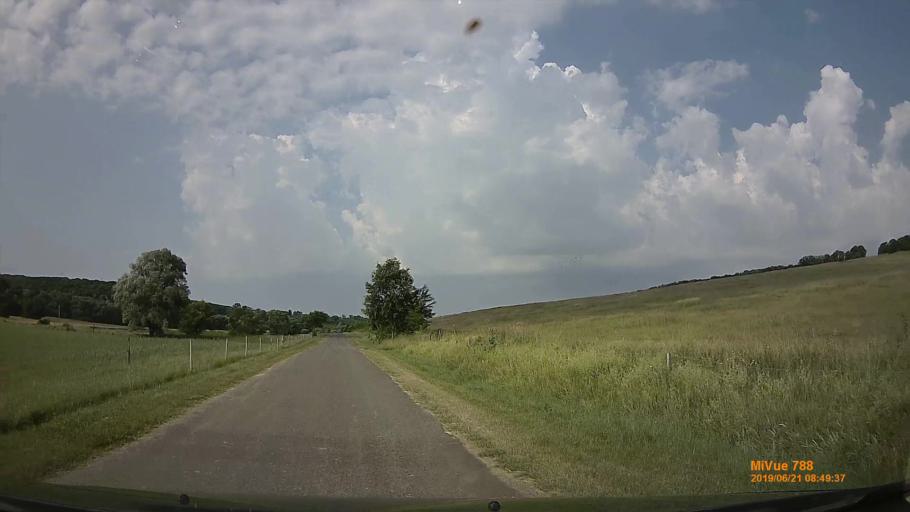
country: HU
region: Baranya
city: Buekkoesd
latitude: 46.1827
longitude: 17.9195
